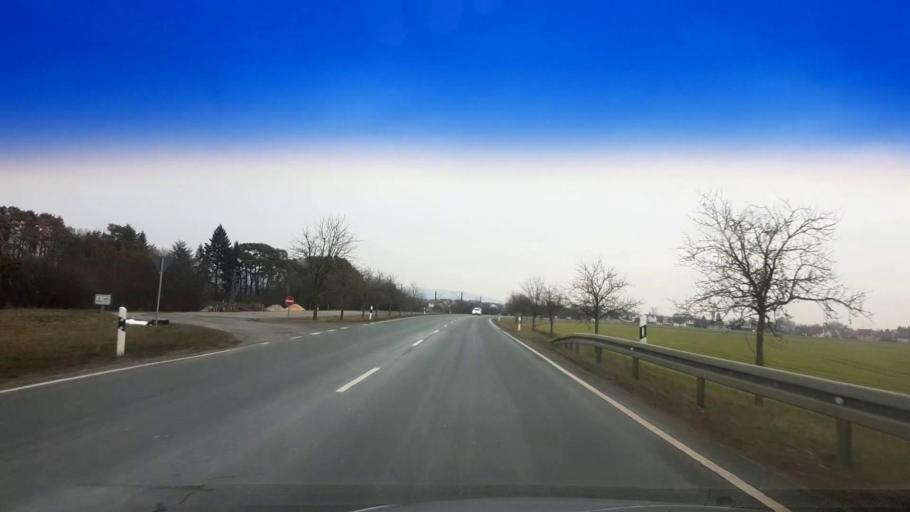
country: DE
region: Bavaria
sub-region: Upper Franconia
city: Altendorf
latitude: 49.8076
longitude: 11.0029
